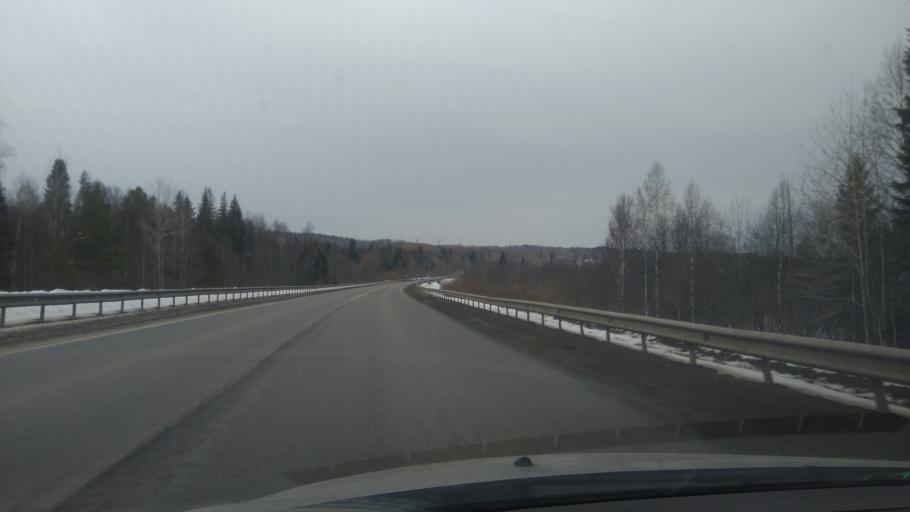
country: RU
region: Sverdlovsk
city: Arti
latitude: 56.7827
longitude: 58.4223
